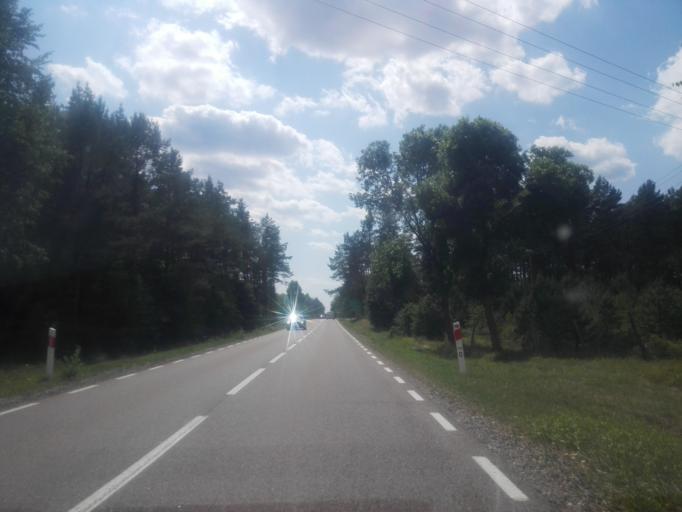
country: PL
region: Podlasie
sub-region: Powiat sejnenski
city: Krasnopol
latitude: 53.9532
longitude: 23.2091
